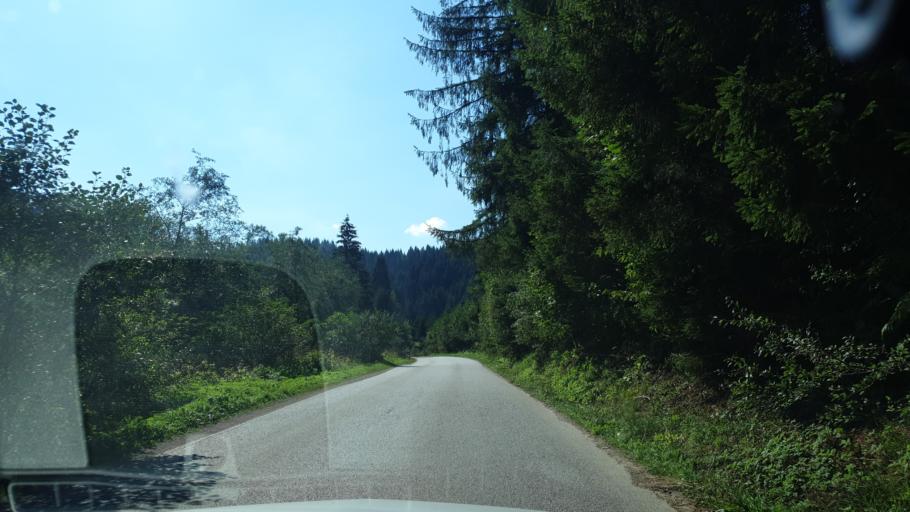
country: RS
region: Central Serbia
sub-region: Zlatiborski Okrug
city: Nova Varos
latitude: 43.4537
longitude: 19.8426
